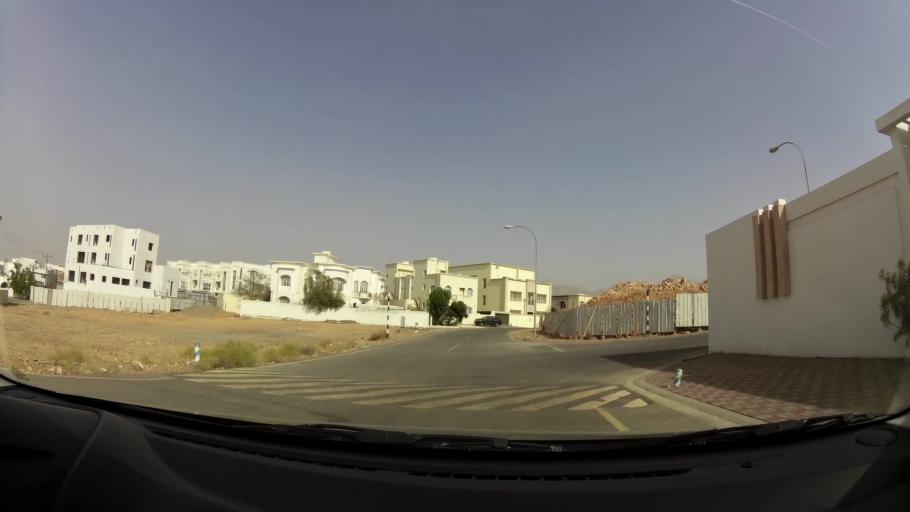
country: OM
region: Muhafazat Masqat
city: Bawshar
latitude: 23.5608
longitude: 58.3606
